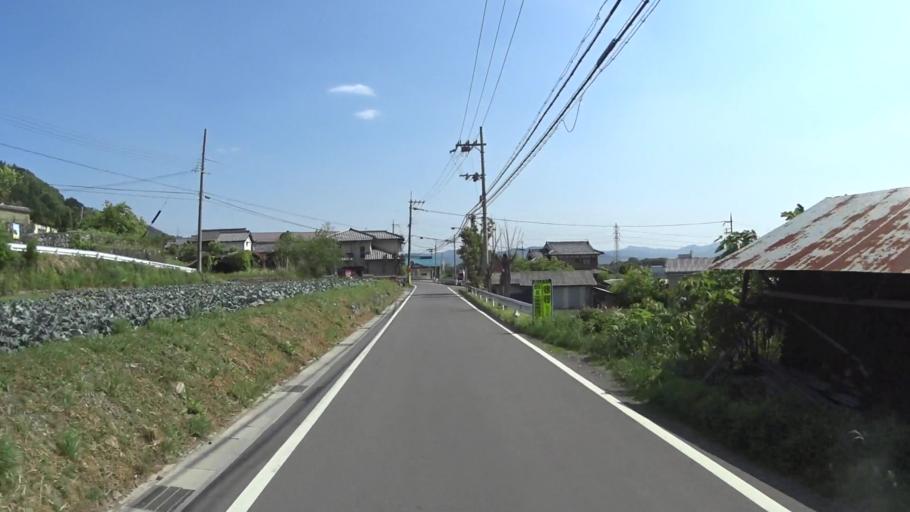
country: JP
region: Kyoto
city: Kameoka
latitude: 35.0543
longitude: 135.5796
